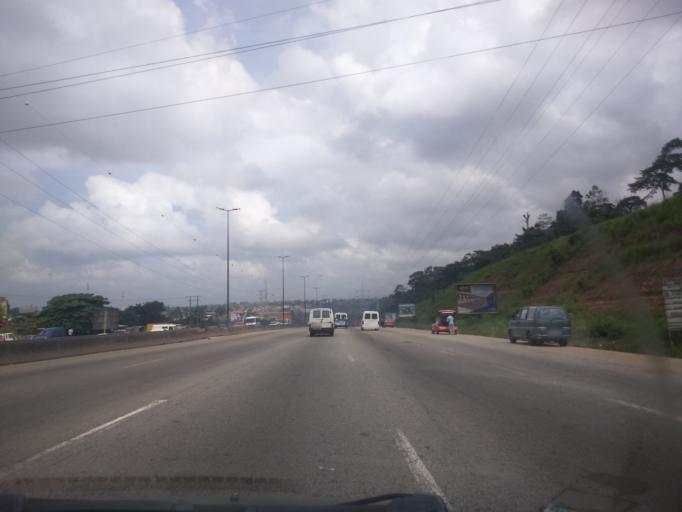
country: CI
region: Lagunes
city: Abobo
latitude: 5.3640
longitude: -4.0315
